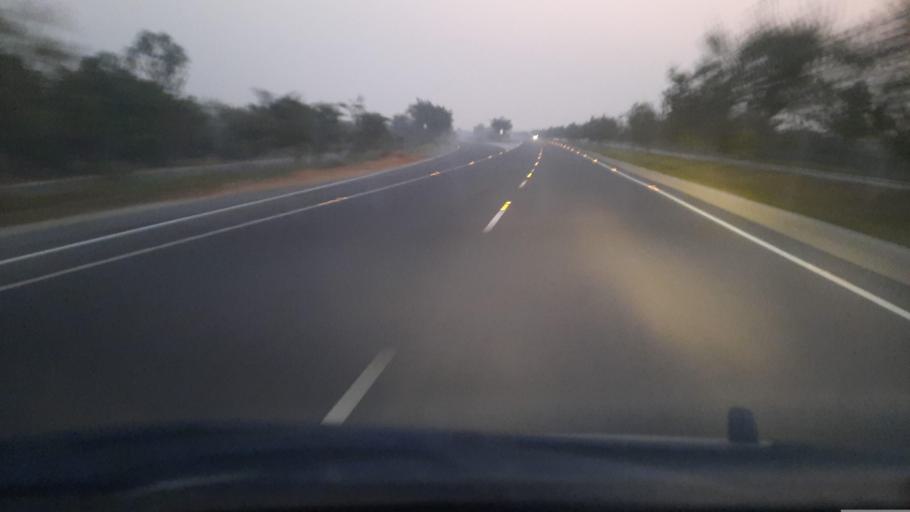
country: BD
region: Dhaka
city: Char Bhadrasan
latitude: 23.3982
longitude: 90.2373
